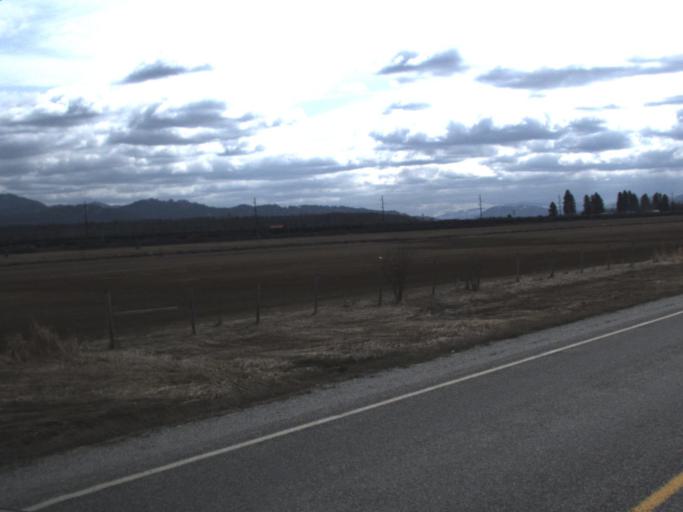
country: US
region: Washington
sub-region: Pend Oreille County
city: Newport
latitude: 48.3299
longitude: -117.3005
